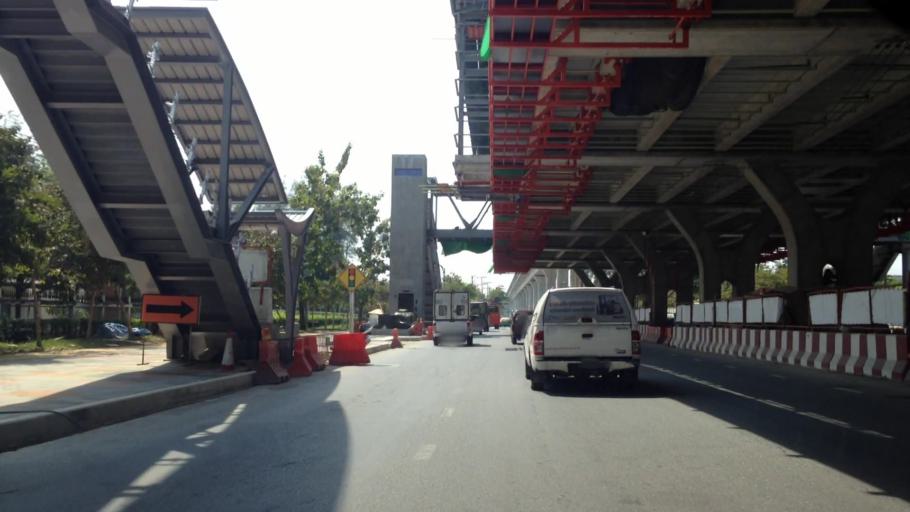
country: TH
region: Bangkok
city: Sai Mai
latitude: 13.9252
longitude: 100.6262
